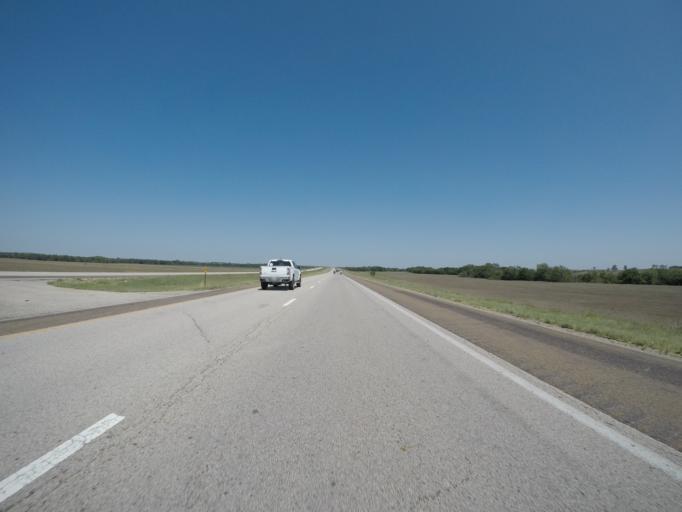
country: US
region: Kansas
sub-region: Saline County
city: Salina
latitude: 38.8782
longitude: -97.8161
